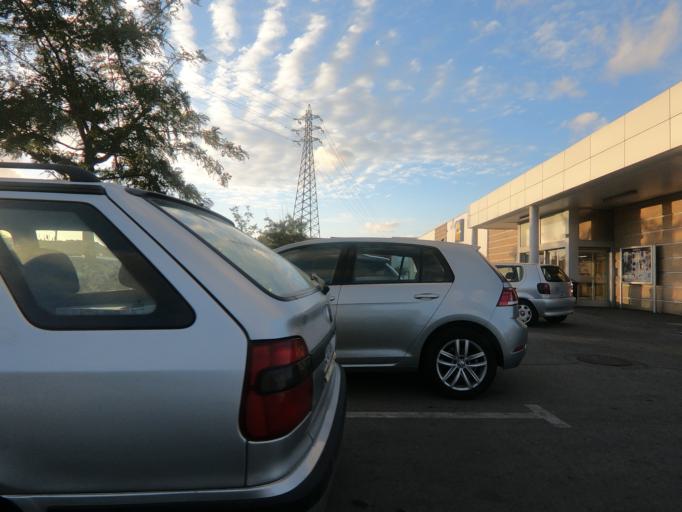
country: PT
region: Setubal
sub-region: Moita
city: Alhos Vedros
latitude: 38.6564
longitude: -9.0364
